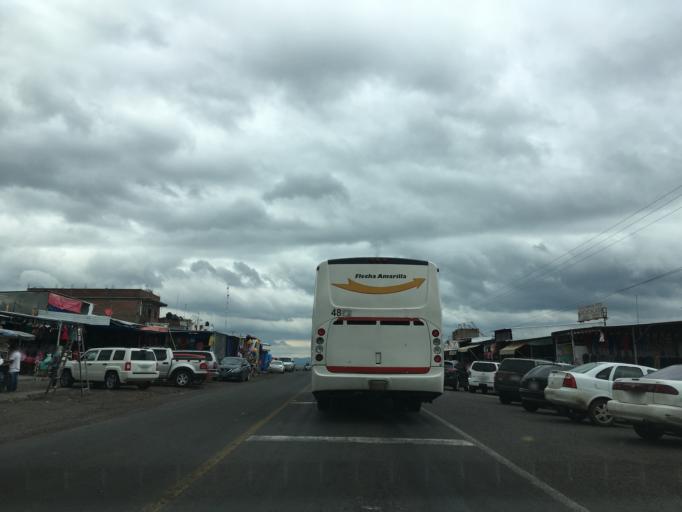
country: MX
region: Michoacan
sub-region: Cuitzeo
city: Cuamio
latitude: 20.0579
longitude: -101.1502
